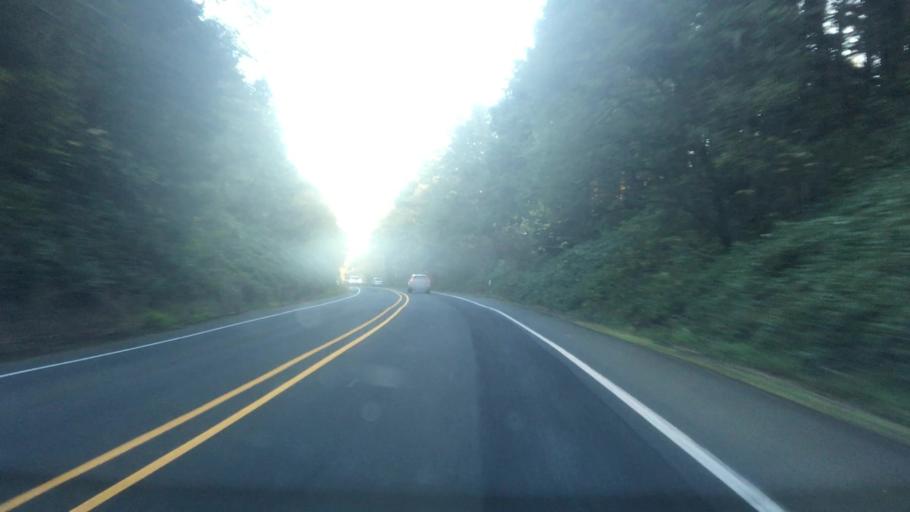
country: US
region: Oregon
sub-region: Clatsop County
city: Cannon Beach
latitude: 45.8830
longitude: -123.9592
